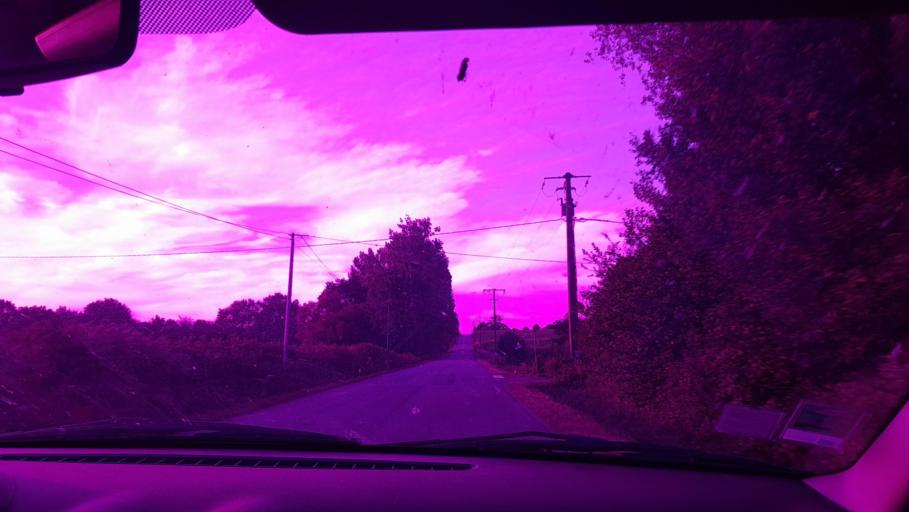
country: FR
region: Brittany
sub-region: Departement d'Ille-et-Vilaine
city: Le Pertre
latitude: 47.9953
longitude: -1.0402
